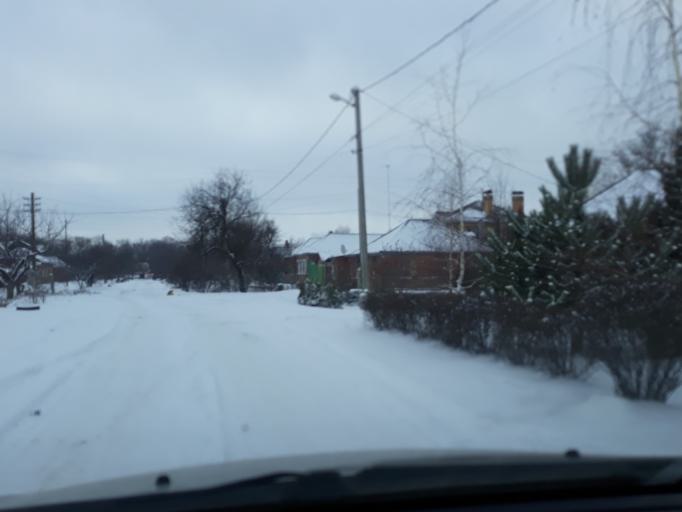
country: RU
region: Rostov
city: Taganrog
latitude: 47.2299
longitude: 38.8915
